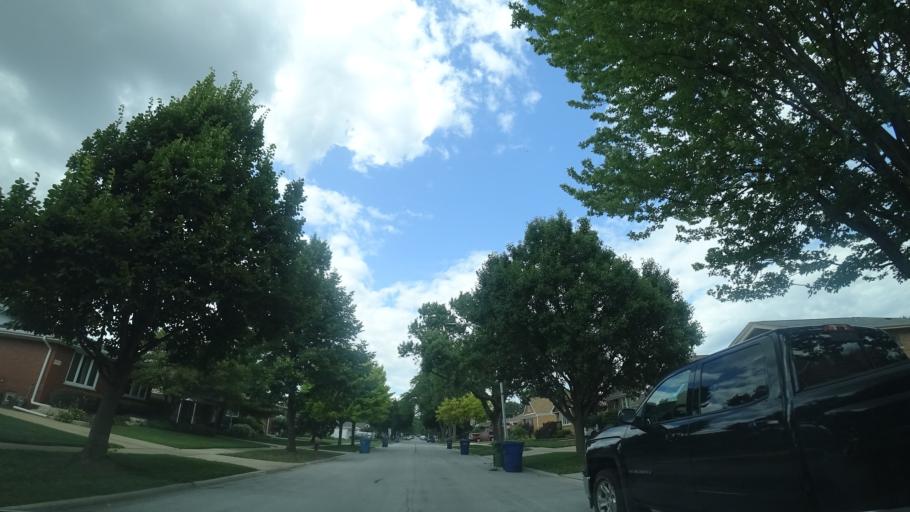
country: US
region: Illinois
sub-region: Cook County
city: Oak Lawn
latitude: 41.6972
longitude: -87.7327
